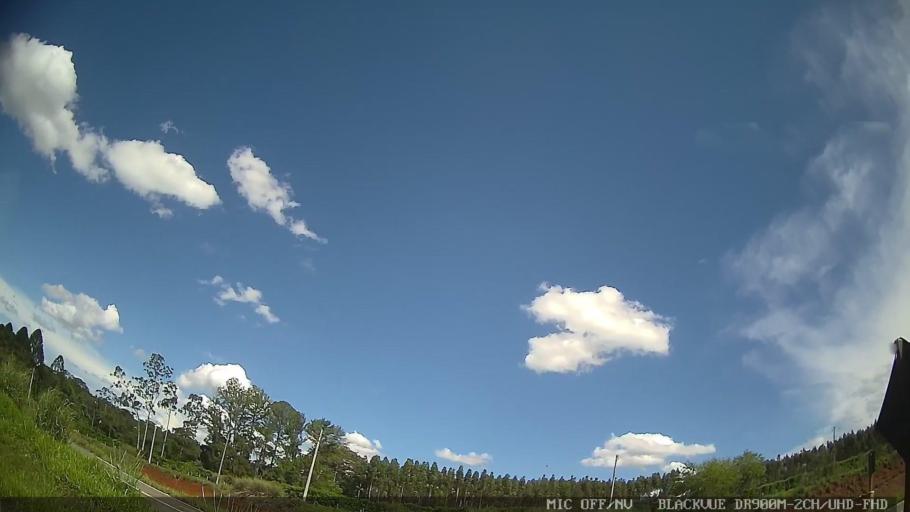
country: BR
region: Sao Paulo
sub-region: Pedreira
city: Pedreira
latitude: -22.7273
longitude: -46.8531
